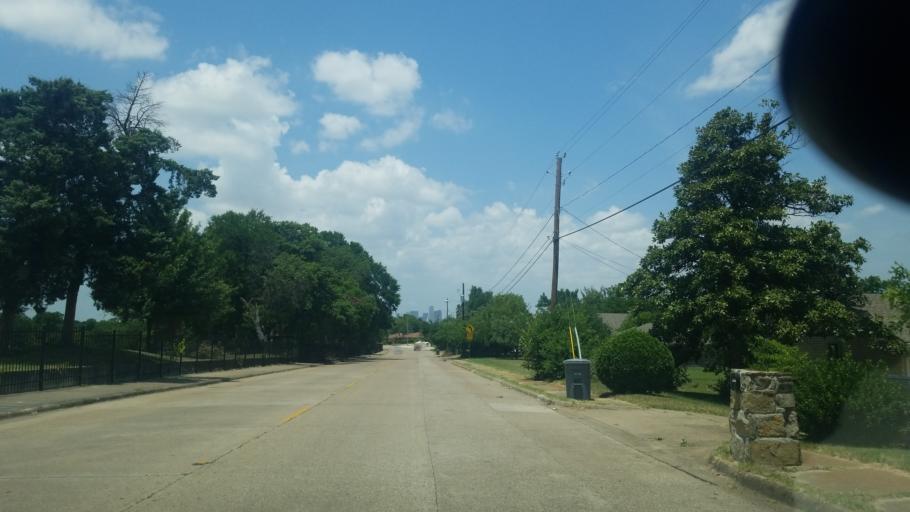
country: US
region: Texas
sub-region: Dallas County
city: Dallas
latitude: 32.7231
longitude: -96.7872
